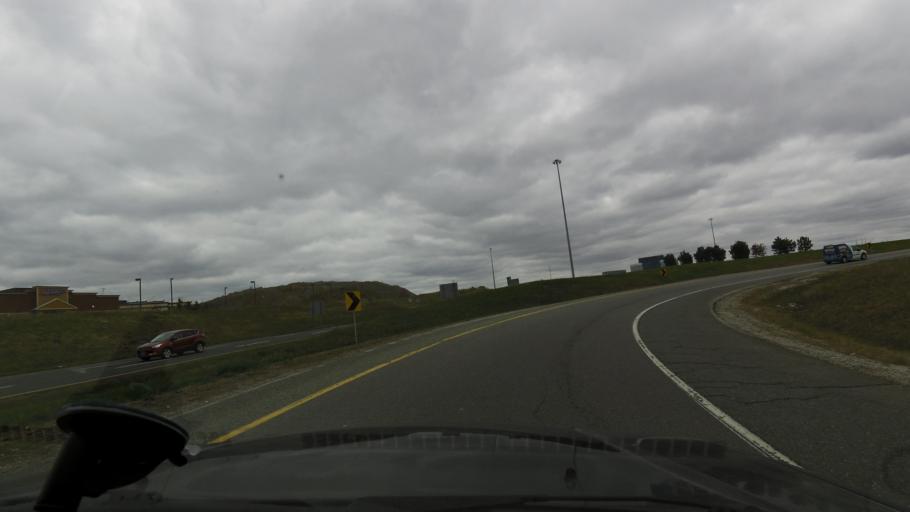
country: CA
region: Ontario
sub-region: York
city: Richmond Hill
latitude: 43.8474
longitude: -79.3731
